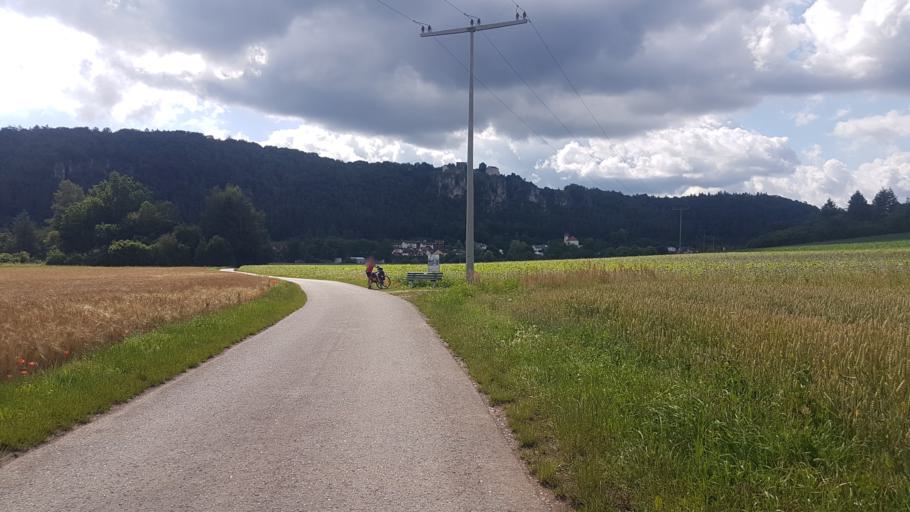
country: DE
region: Bavaria
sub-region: Upper Bavaria
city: Bohmfeld
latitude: 48.9329
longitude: 11.3686
